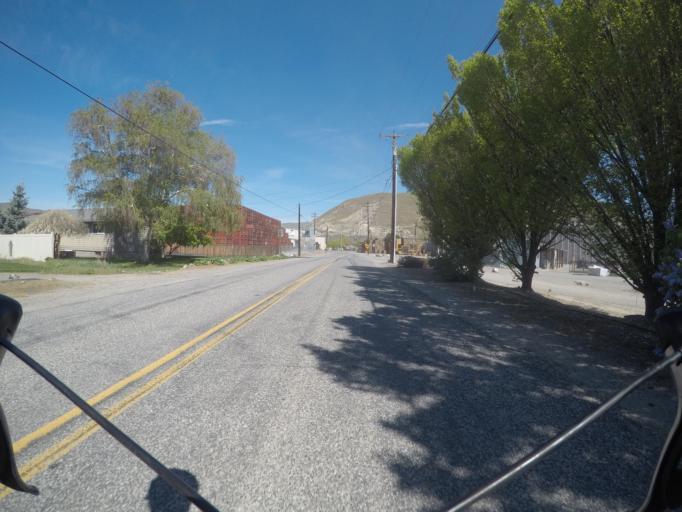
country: US
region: Washington
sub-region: Chelan County
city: Cashmere
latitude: 47.4858
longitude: -120.4180
